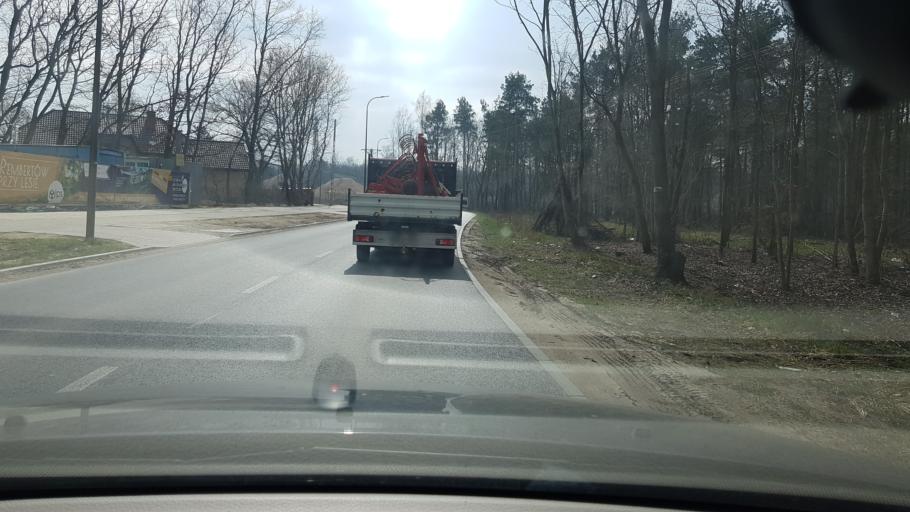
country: PL
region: Masovian Voivodeship
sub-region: Warszawa
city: Rembertow
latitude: 52.2601
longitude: 21.1516
